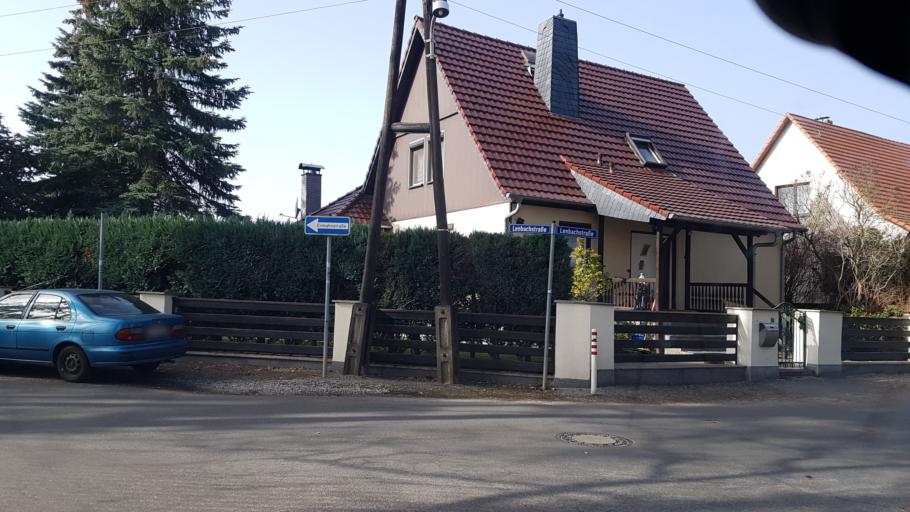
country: DE
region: Brandenburg
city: Cottbus
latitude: 51.7554
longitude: 14.3659
